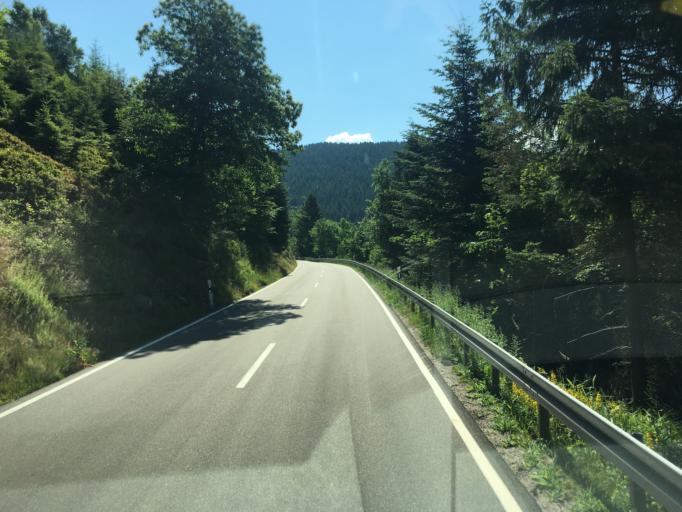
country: DE
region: Baden-Wuerttemberg
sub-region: Freiburg Region
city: Seebach
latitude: 48.5731
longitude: 8.2159
